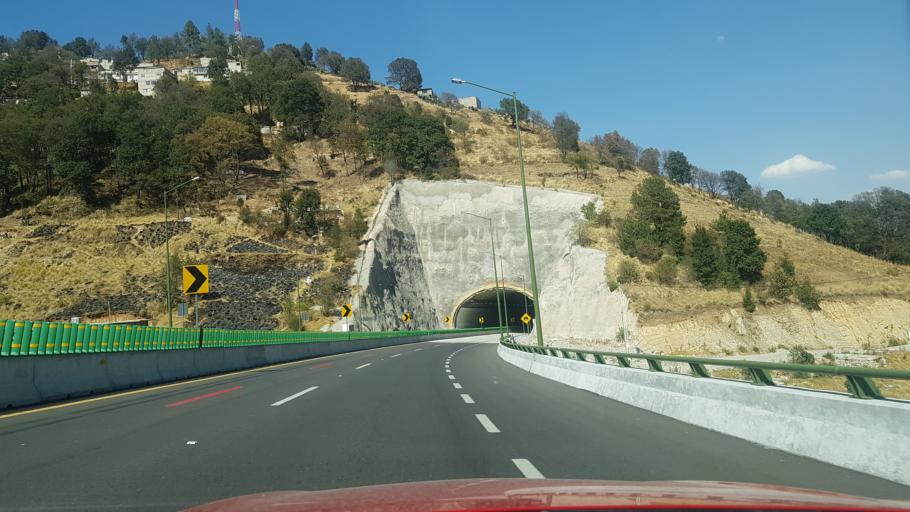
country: MX
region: Mexico
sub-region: Naucalpan de Juarez
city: San Francisco Chimalpa
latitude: 19.4334
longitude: -99.3415
